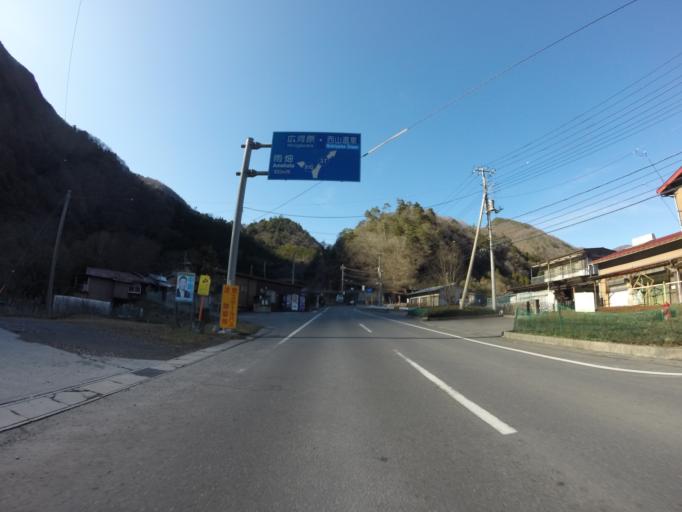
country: JP
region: Yamanashi
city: Ryuo
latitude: 35.4109
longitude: 138.3583
